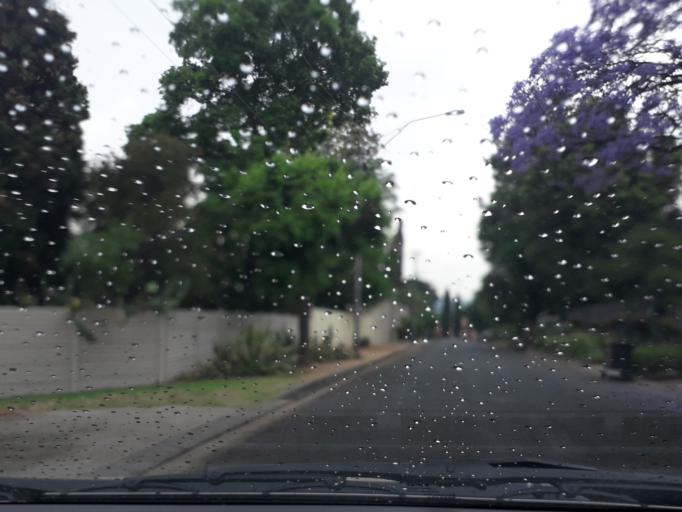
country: ZA
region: Gauteng
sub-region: City of Johannesburg Metropolitan Municipality
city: Modderfontein
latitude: -26.1335
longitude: 28.0994
